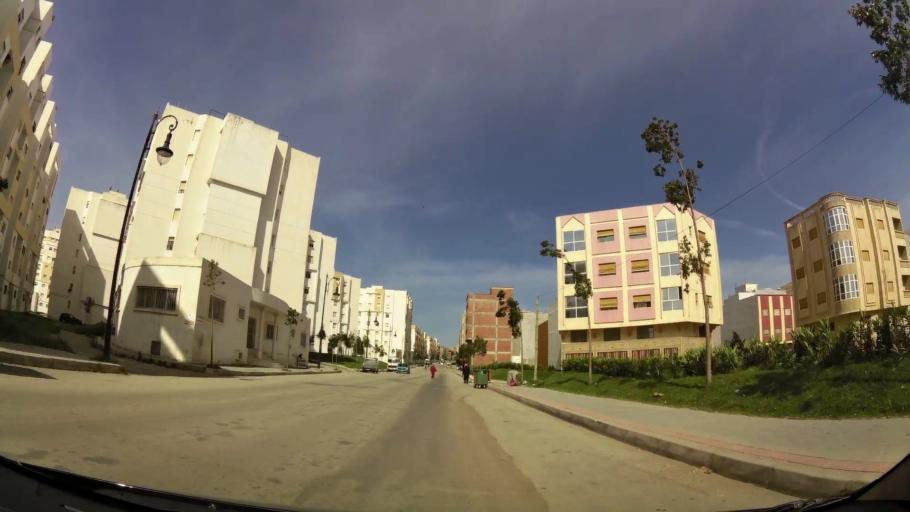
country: MA
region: Tanger-Tetouan
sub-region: Tanger-Assilah
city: Tangier
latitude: 35.7237
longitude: -5.8056
